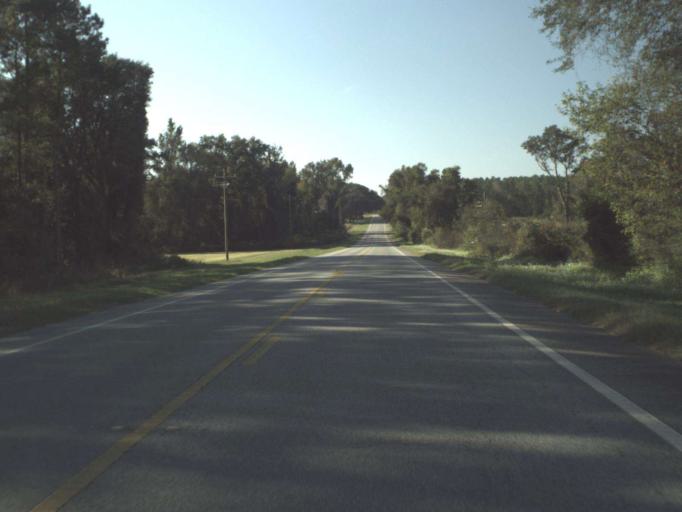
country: US
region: Georgia
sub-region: Brooks County
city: Quitman
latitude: 30.6322
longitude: -83.6455
